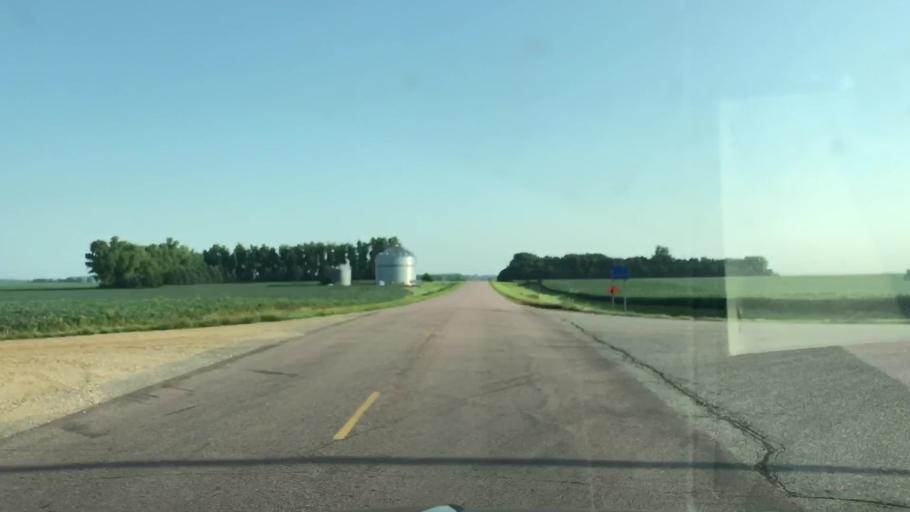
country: US
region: Iowa
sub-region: Lyon County
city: George
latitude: 43.3163
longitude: -95.9990
